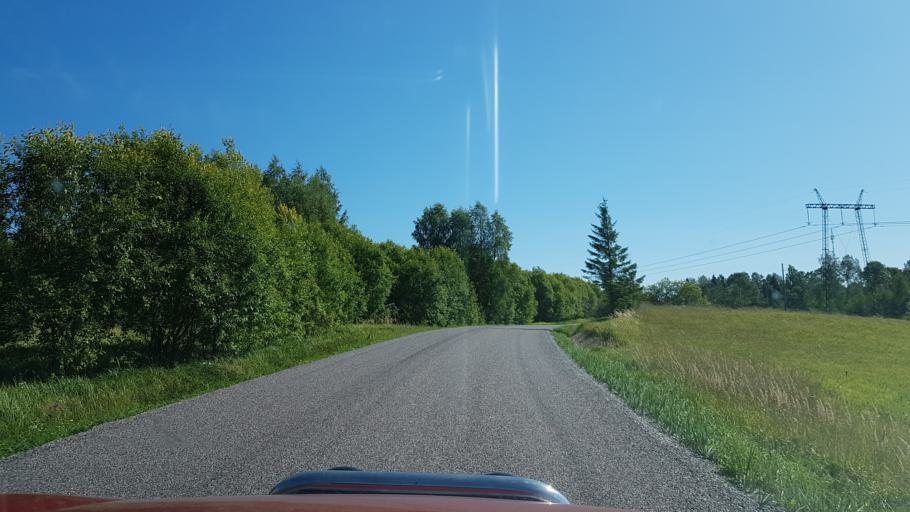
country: EE
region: Tartu
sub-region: Elva linn
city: Elva
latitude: 58.2447
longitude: 26.3910
